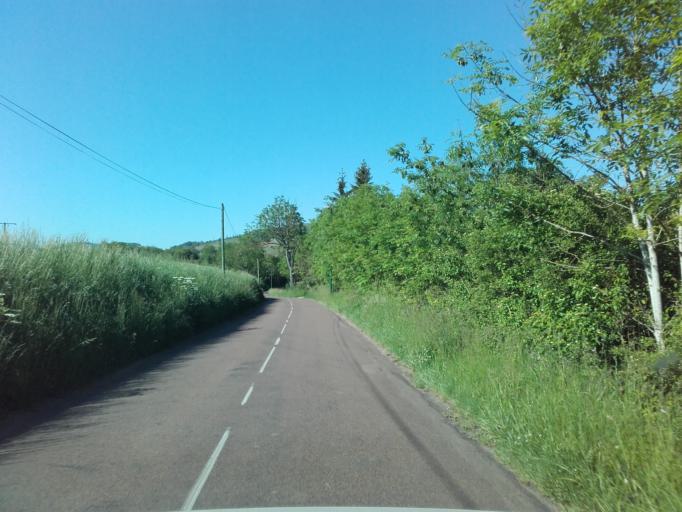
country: FR
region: Bourgogne
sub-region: Departement de la Cote-d'Or
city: Nolay
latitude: 46.9471
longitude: 4.6318
